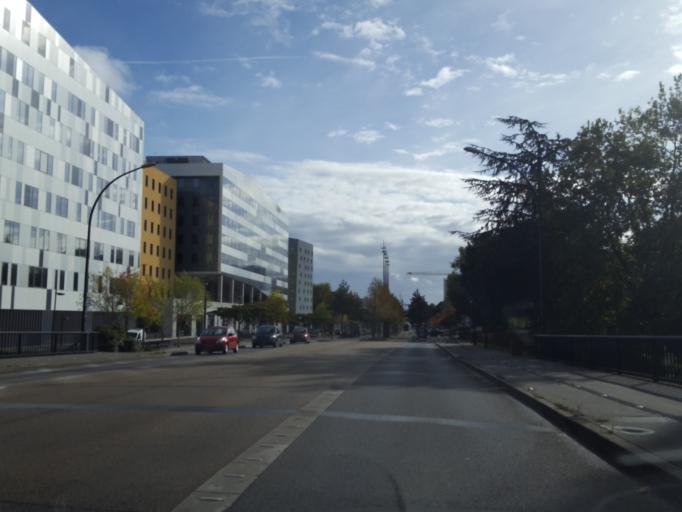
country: FR
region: Pays de la Loire
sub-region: Departement de la Loire-Atlantique
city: Nantes
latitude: 47.2094
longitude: -1.5415
